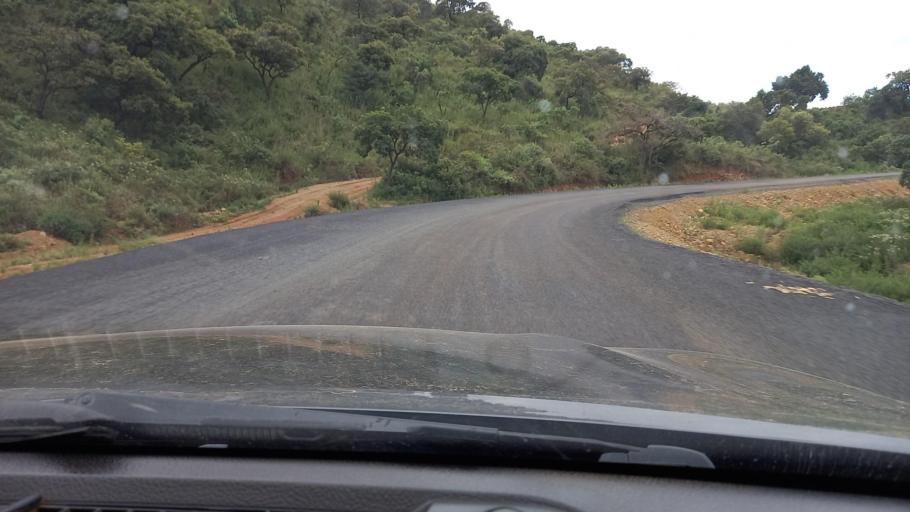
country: ET
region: Southern Nations, Nationalities, and People's Region
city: Mizan Teferi
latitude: 6.2068
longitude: 35.6536
